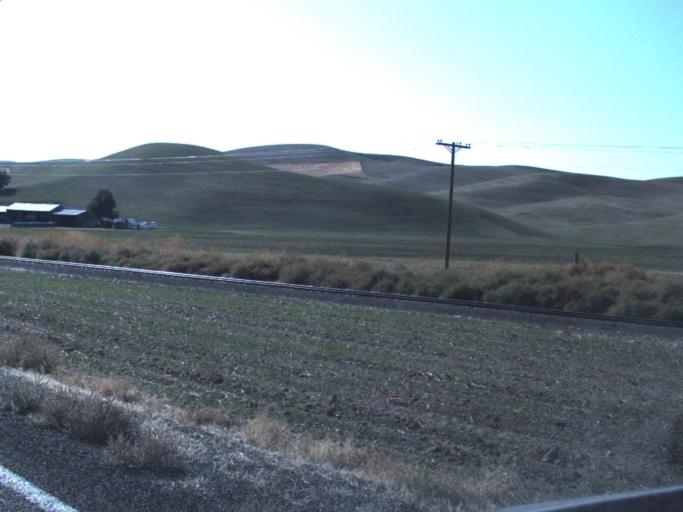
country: US
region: Washington
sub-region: Walla Walla County
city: Walla Walla
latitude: 46.2187
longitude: -118.3927
